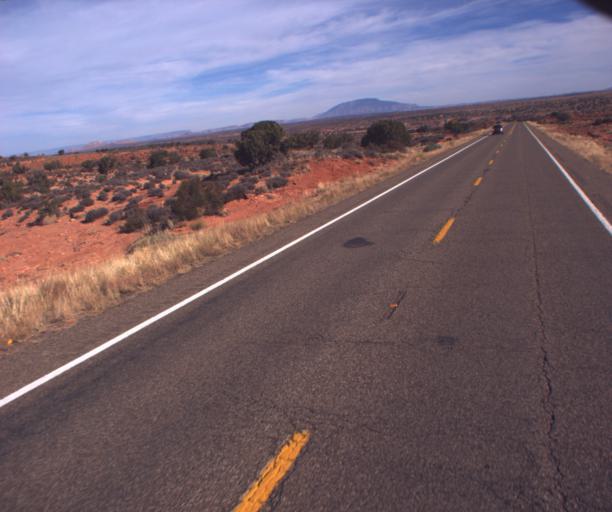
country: US
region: Arizona
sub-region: Coconino County
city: Kaibito
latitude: 36.6010
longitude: -111.0907
